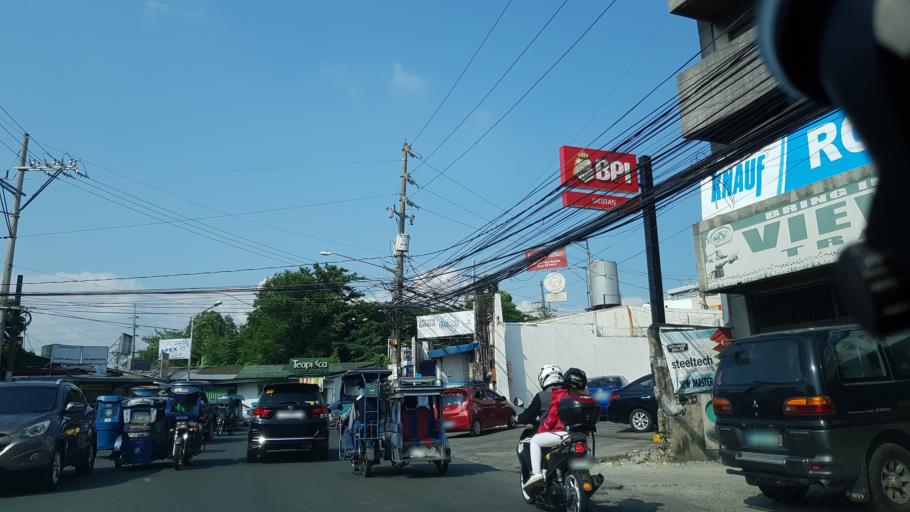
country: PH
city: Sambayanihan People's Village
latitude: 14.4842
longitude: 121.0380
